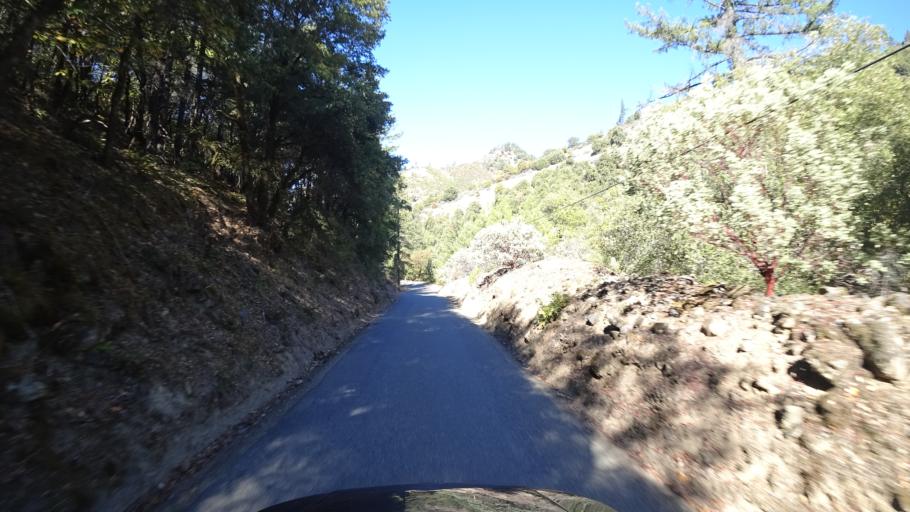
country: US
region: California
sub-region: Humboldt County
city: Willow Creek
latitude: 41.2552
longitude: -123.3177
